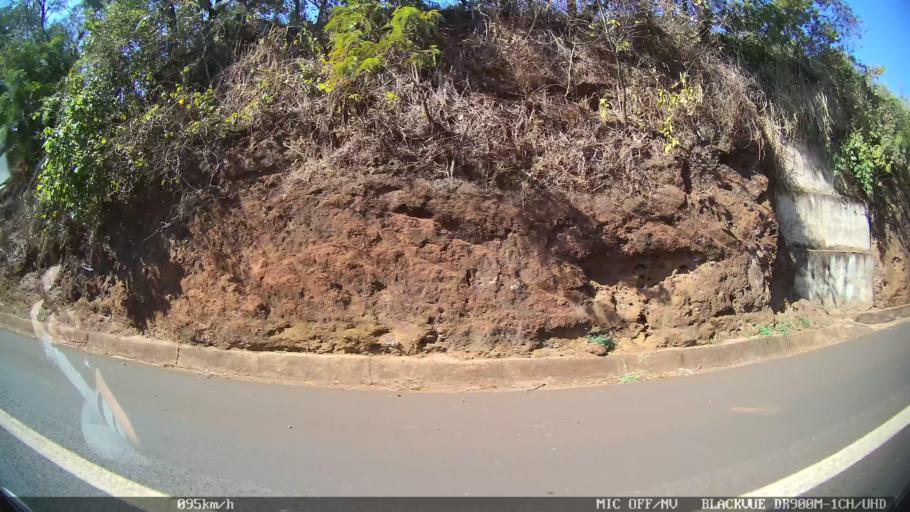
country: BR
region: Sao Paulo
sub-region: Batatais
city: Batatais
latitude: -20.7371
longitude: -47.5300
